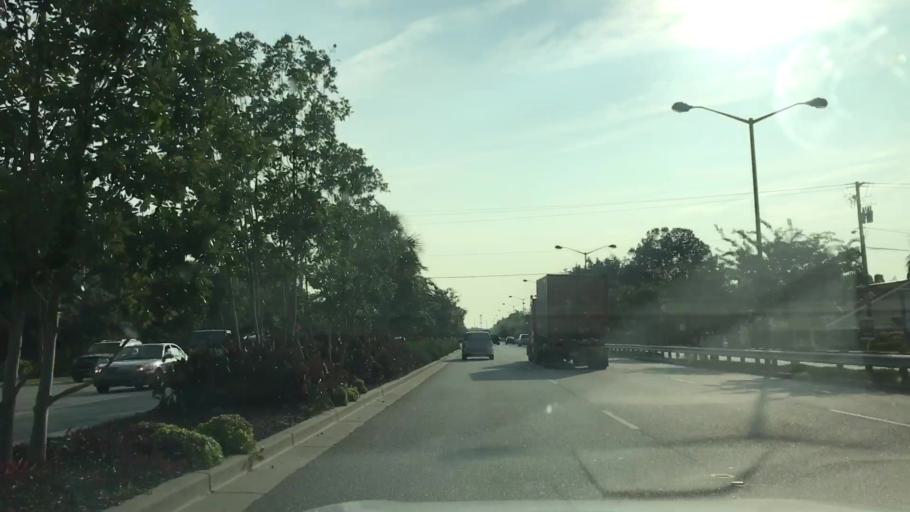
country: US
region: South Carolina
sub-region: Charleston County
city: Mount Pleasant
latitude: 32.8086
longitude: -79.8770
